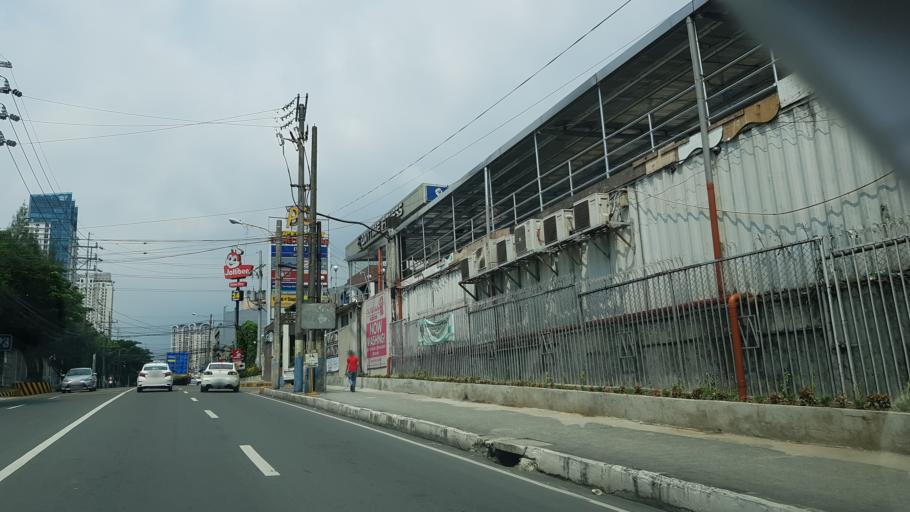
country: PH
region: Metro Manila
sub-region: Pasig
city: Pasig City
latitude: 14.5738
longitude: 121.0571
